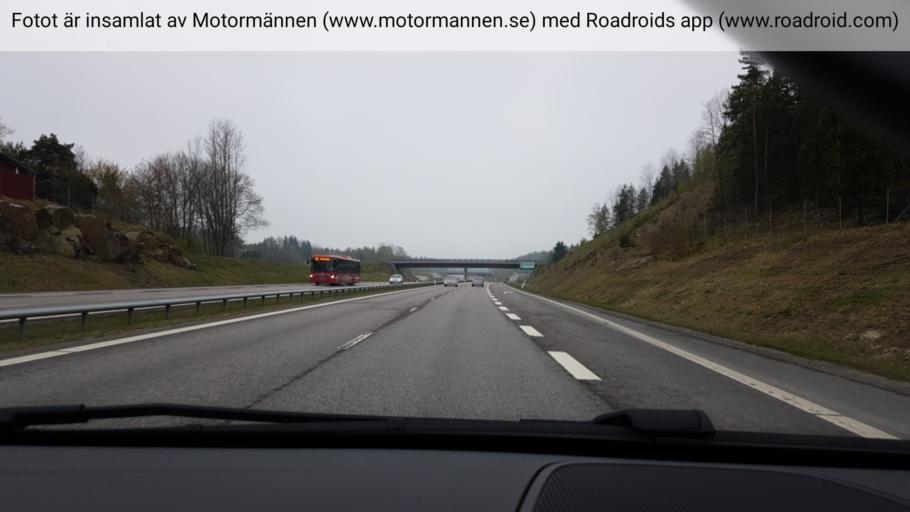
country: SE
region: Stockholm
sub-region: Nynashamns Kommun
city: Osmo
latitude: 59.0006
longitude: 17.9378
